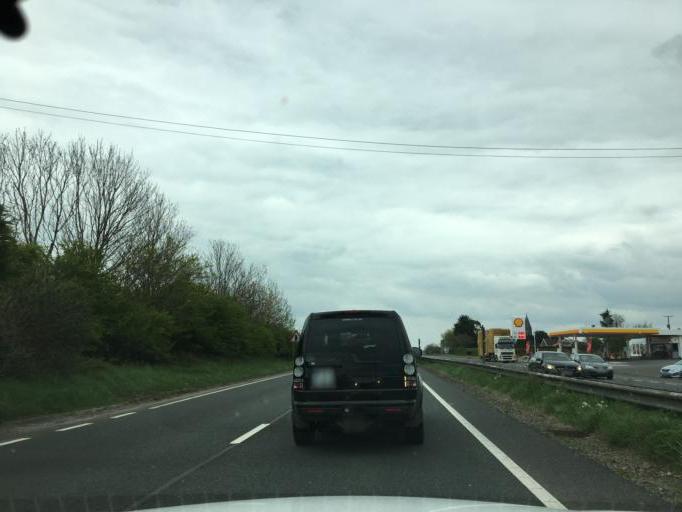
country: GB
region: Wales
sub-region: Carmarthenshire
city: Saint Clears
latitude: 51.8252
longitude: -4.4727
